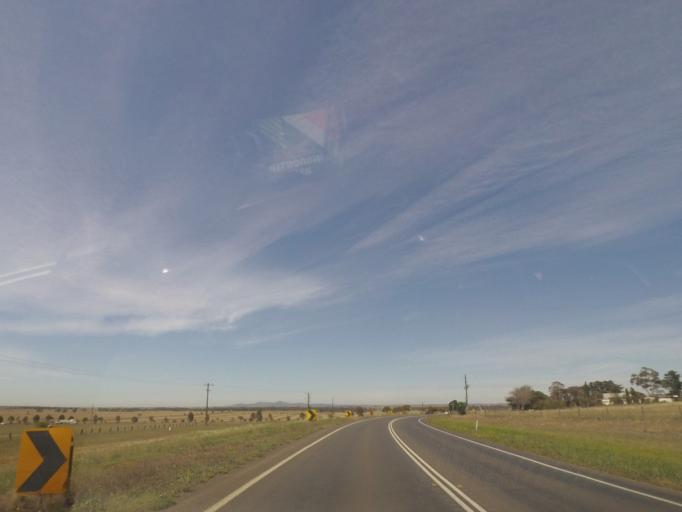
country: AU
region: Victoria
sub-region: Moorabool
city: Bacchus Marsh
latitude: -37.7742
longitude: 144.4386
